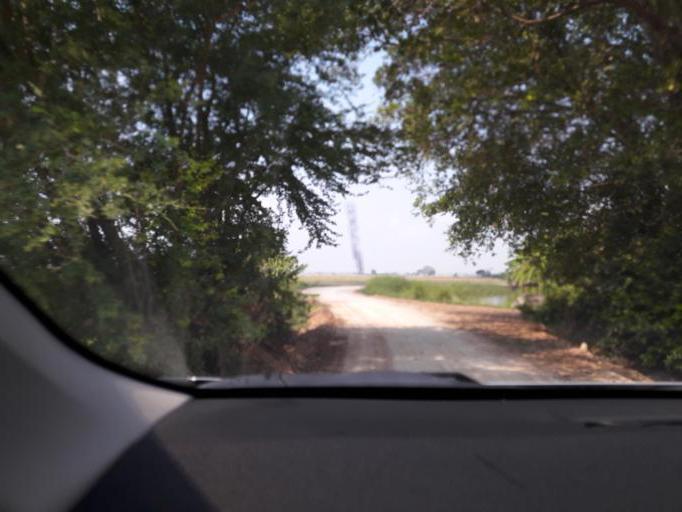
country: TH
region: Ang Thong
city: Ang Thong
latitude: 14.5611
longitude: 100.4185
